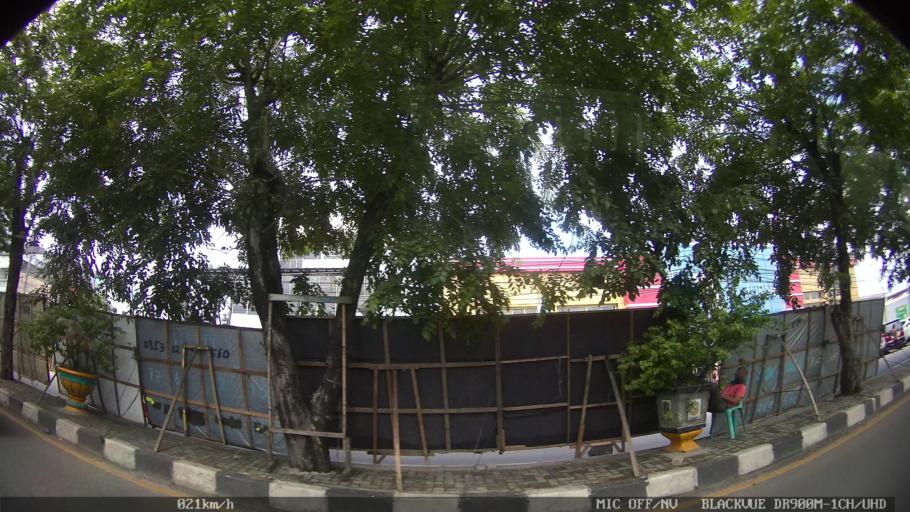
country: ID
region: North Sumatra
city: Medan
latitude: 3.6132
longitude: 98.7071
